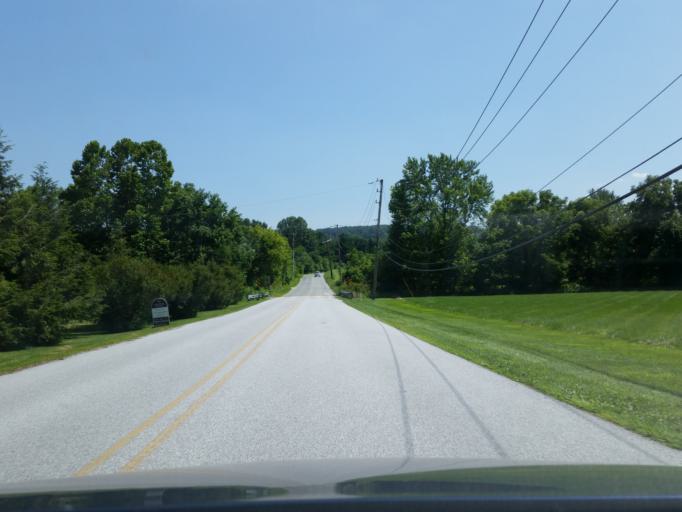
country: US
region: Pennsylvania
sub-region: York County
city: Stonybrook
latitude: 39.9888
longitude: -76.6260
